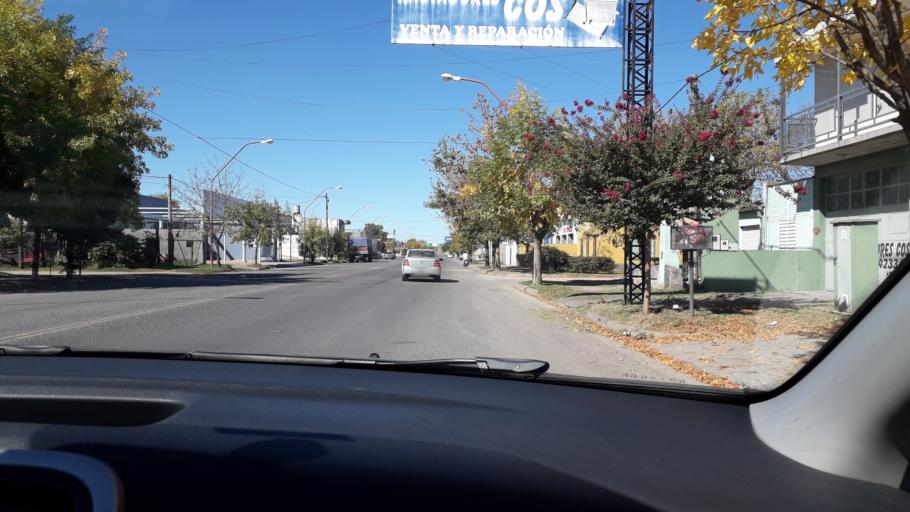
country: AR
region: Buenos Aires
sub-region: Partido de Azul
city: Azul
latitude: -36.7885
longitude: -59.8451
